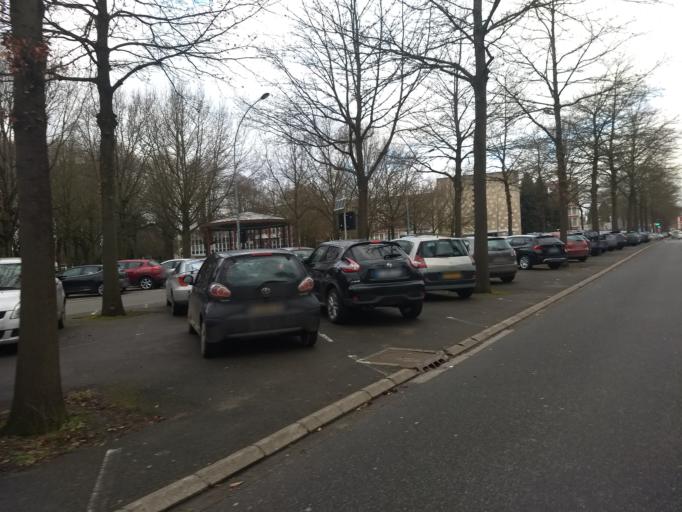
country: FR
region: Nord-Pas-de-Calais
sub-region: Departement du Pas-de-Calais
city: Achicourt
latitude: 50.2865
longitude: 2.7672
